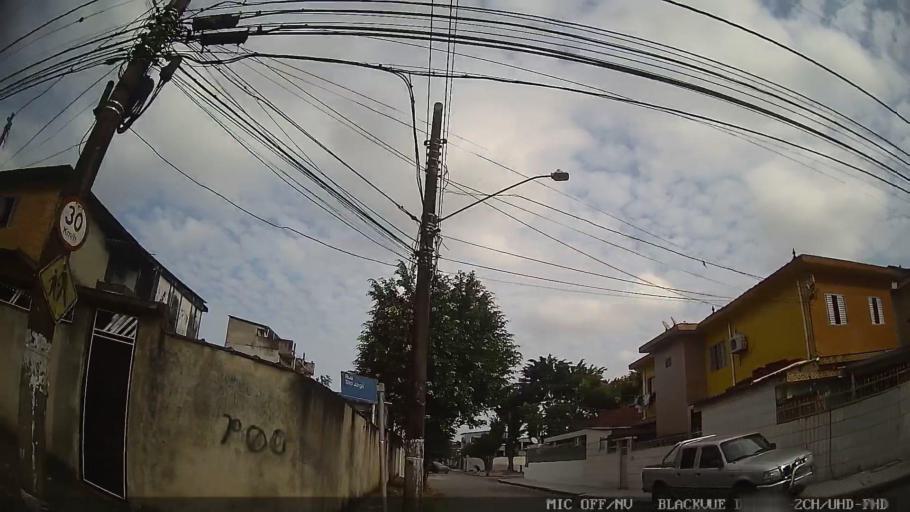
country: BR
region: Sao Paulo
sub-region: Santos
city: Santos
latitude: -23.9488
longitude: -46.2881
